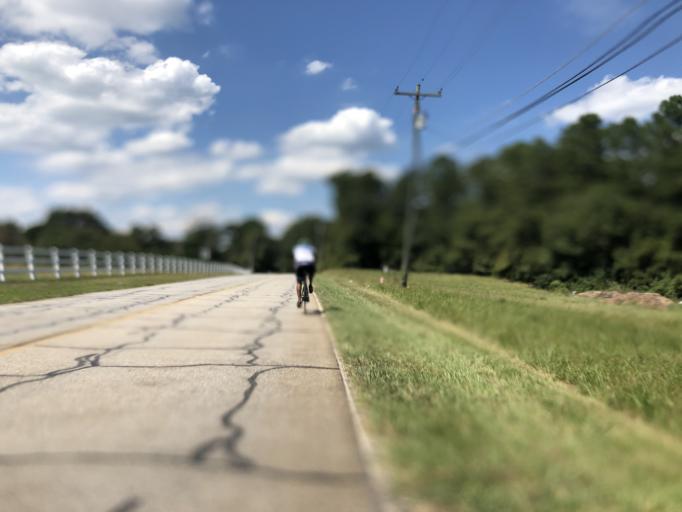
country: US
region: Georgia
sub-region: Fulton County
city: Palmetto
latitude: 33.5265
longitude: -84.6842
